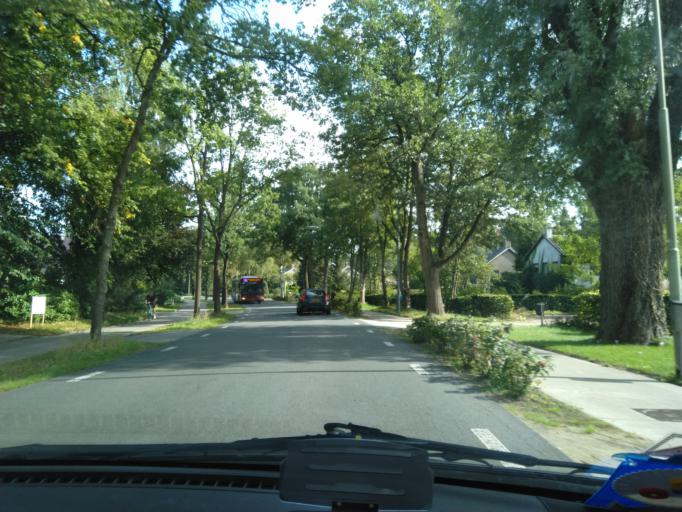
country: NL
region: Groningen
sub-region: Gemeente Groningen
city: Groningen
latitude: 53.1707
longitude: 6.5490
